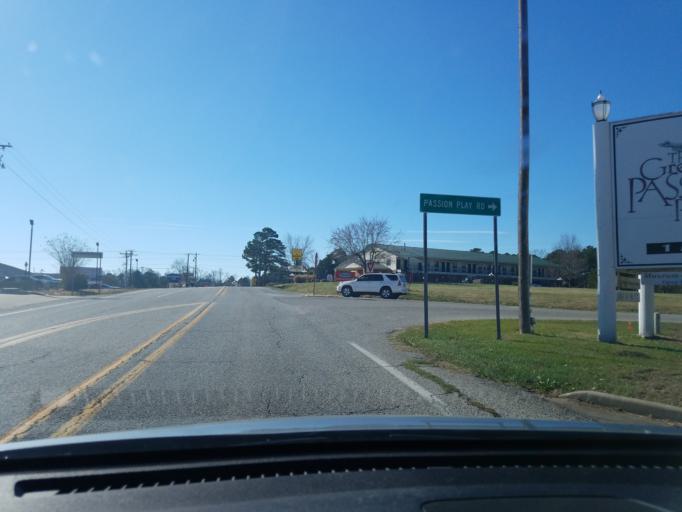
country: US
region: Arkansas
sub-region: Carroll County
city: Eureka Springs
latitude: 36.3924
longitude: -93.7087
